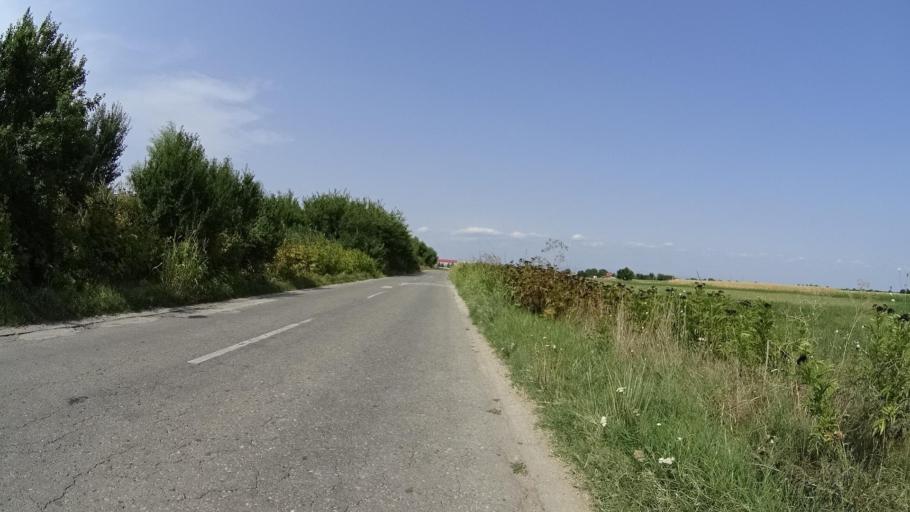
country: BG
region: Plovdiv
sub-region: Obshtina Plovdiv
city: Plovdiv
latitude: 42.2335
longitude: 24.7865
